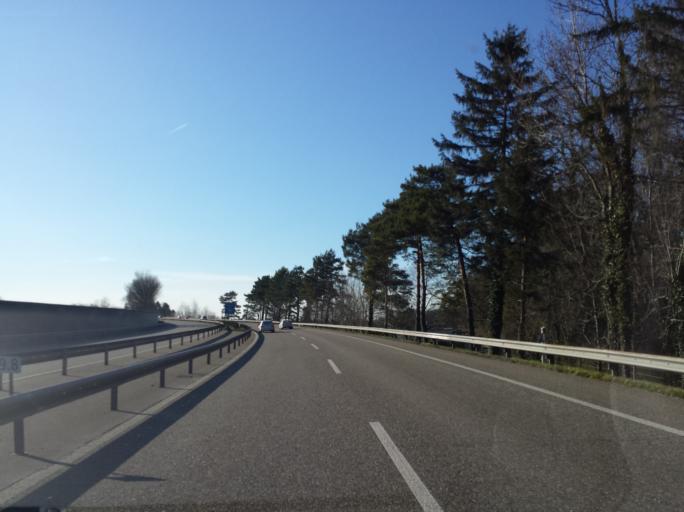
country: CH
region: Saint Gallen
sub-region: Wahlkreis Rheintal
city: Rheineck
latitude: 47.4793
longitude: 9.5826
